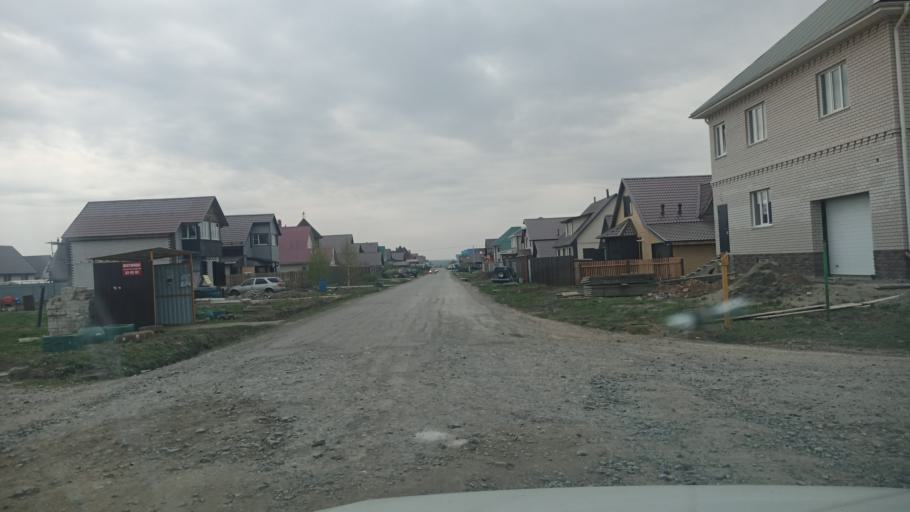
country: RU
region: Altai Krai
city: Yuzhnyy
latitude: 53.2252
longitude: 83.6907
